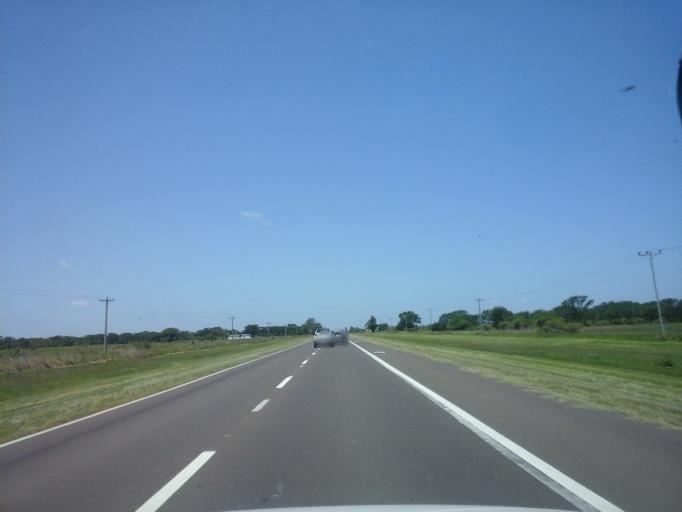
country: AR
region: Corrientes
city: Paso de la Patria
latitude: -27.4126
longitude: -58.6686
